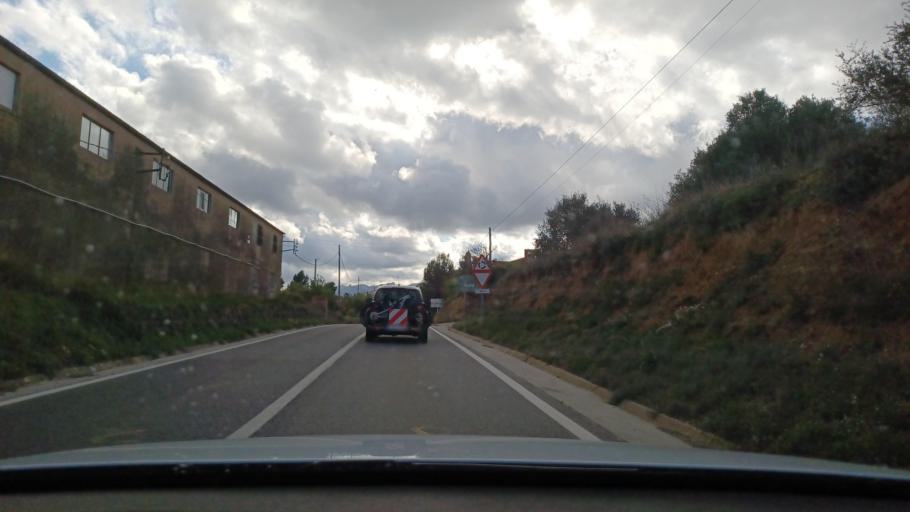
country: ES
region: Catalonia
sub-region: Provincia de Tarragona
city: Botarell
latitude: 41.1373
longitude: 0.9935
